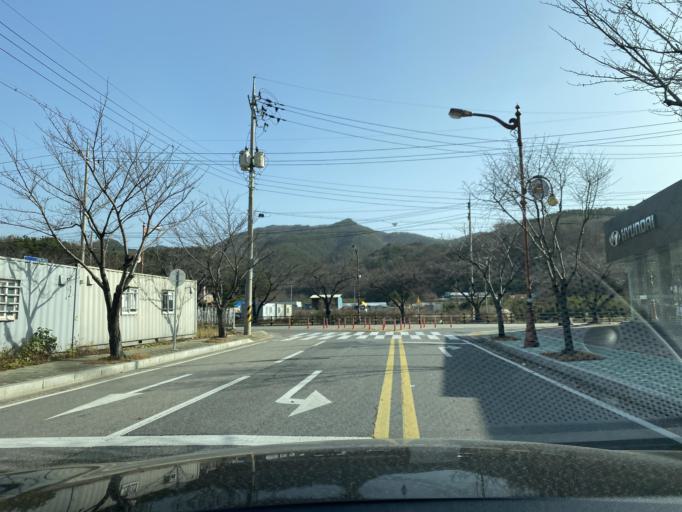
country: KR
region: Chungcheongnam-do
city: Yesan
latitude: 36.6962
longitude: 126.8365
